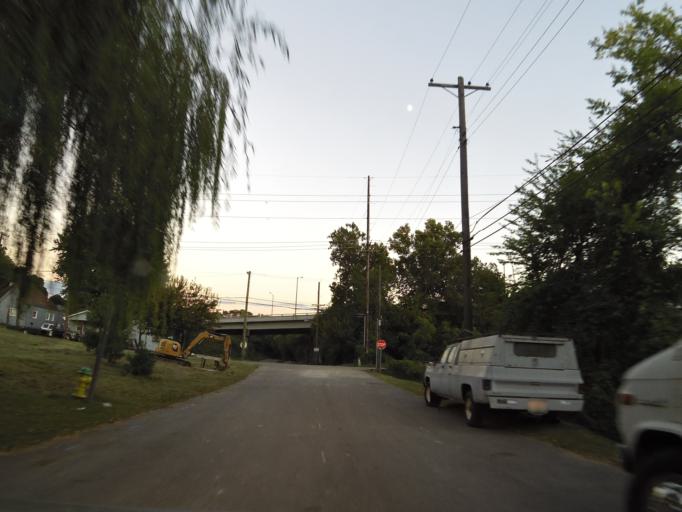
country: US
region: Tennessee
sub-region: Knox County
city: Knoxville
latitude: 35.9831
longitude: -83.9364
